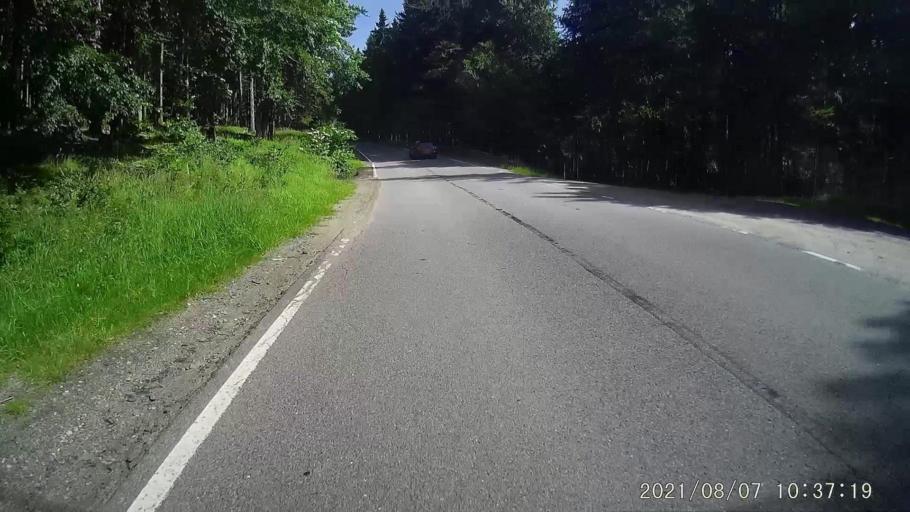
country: PL
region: Lower Silesian Voivodeship
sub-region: Powiat klodzki
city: Duszniki-Zdroj
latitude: 50.3568
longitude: 16.3749
